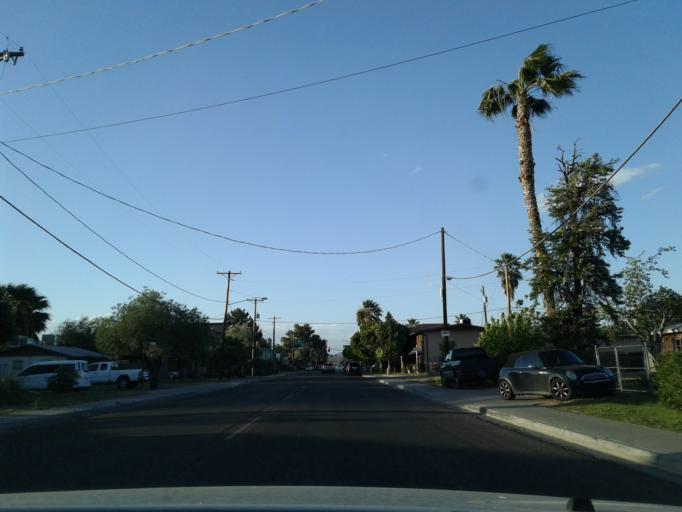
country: US
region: Arizona
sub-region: Maricopa County
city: Phoenix
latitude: 33.5152
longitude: -112.0955
